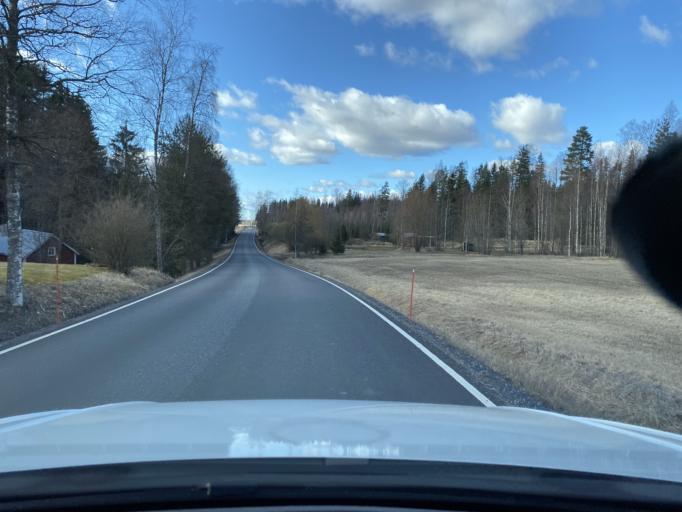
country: FI
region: Pirkanmaa
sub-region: Lounais-Pirkanmaa
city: Punkalaidun
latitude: 61.0749
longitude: 23.2198
